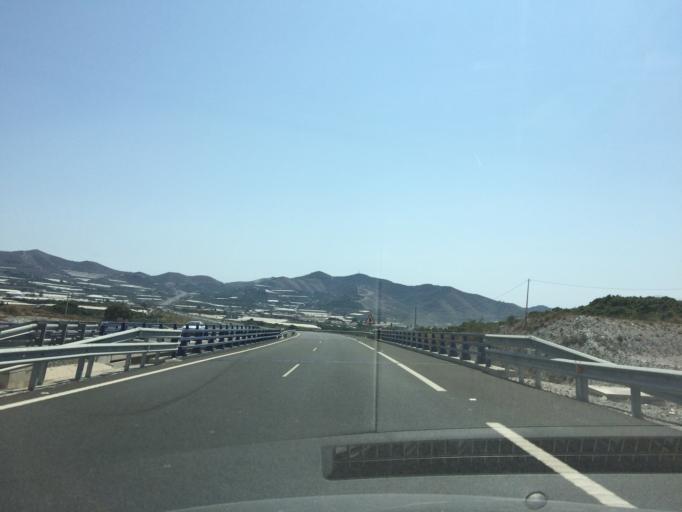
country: ES
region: Andalusia
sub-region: Provincia de Granada
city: Motril
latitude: 36.7394
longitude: -3.4861
